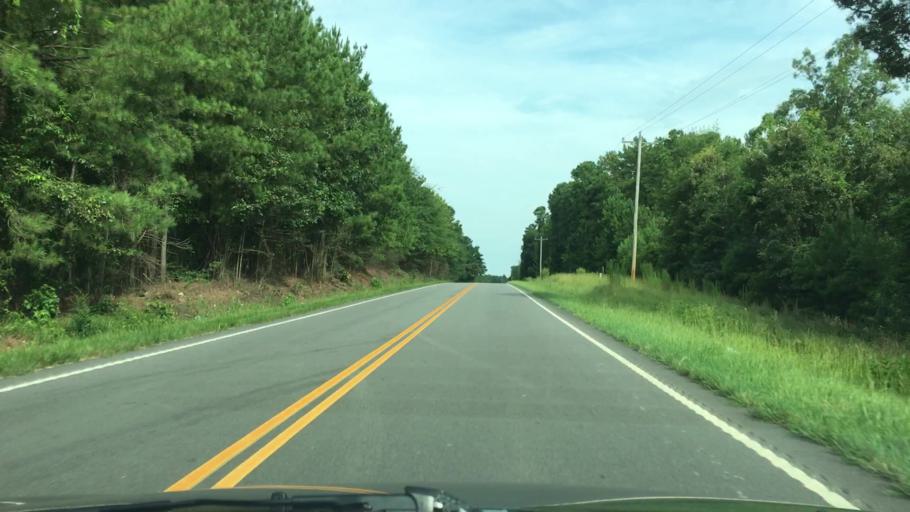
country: US
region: South Carolina
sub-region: Lexington County
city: Batesburg-Leesville
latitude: 33.7067
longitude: -81.4882
